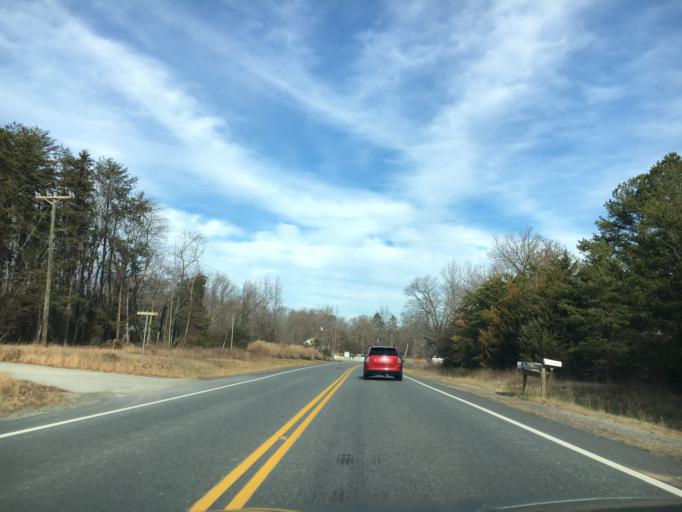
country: US
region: Virginia
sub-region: Louisa County
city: Louisa
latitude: 38.0395
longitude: -77.8869
